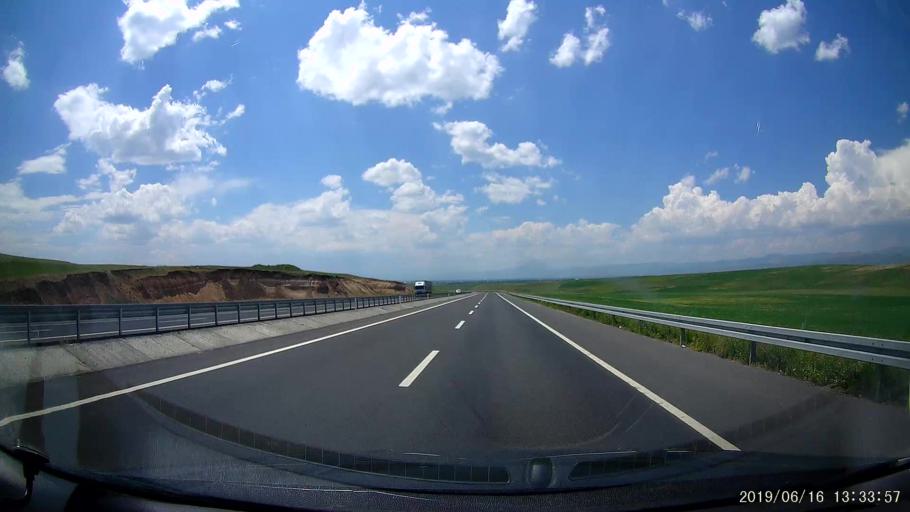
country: TR
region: Agri
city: Agri
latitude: 39.7100
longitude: 43.1405
